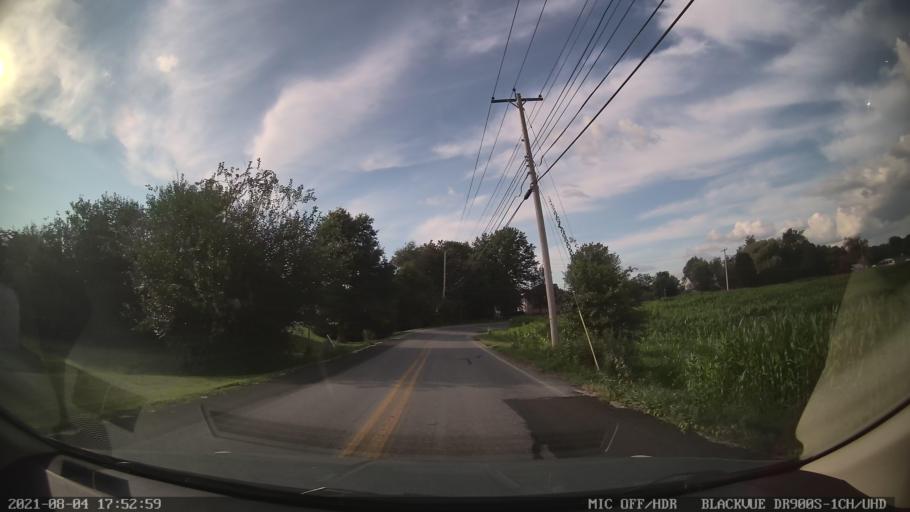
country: US
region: Pennsylvania
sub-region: Berks County
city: Topton
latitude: 40.5160
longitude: -75.6996
